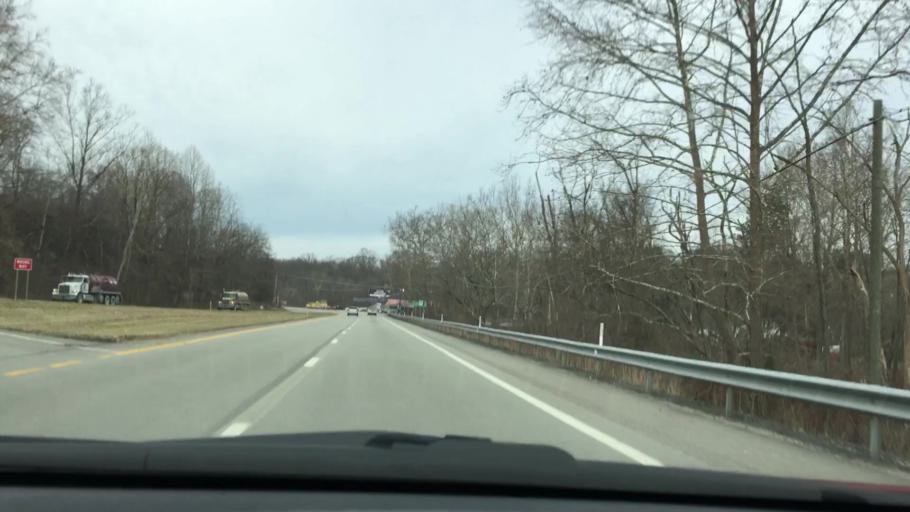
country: US
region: Pennsylvania
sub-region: Fayette County
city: Oliver
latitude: 39.9492
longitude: -79.7342
